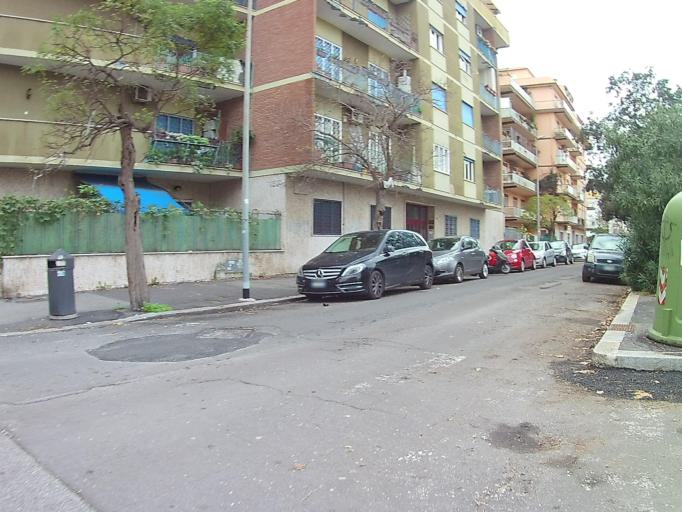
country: IT
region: Latium
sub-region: Citta metropolitana di Roma Capitale
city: Lido di Ostia
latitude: 41.7272
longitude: 12.2912
